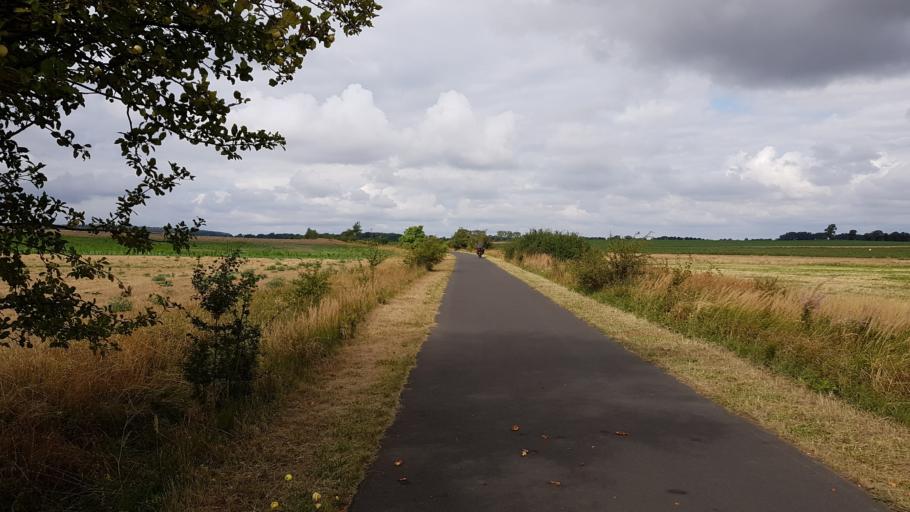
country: PL
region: West Pomeranian Voivodeship
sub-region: Powiat pyrzycki
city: Przelewice
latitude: 53.1341
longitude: 15.0016
